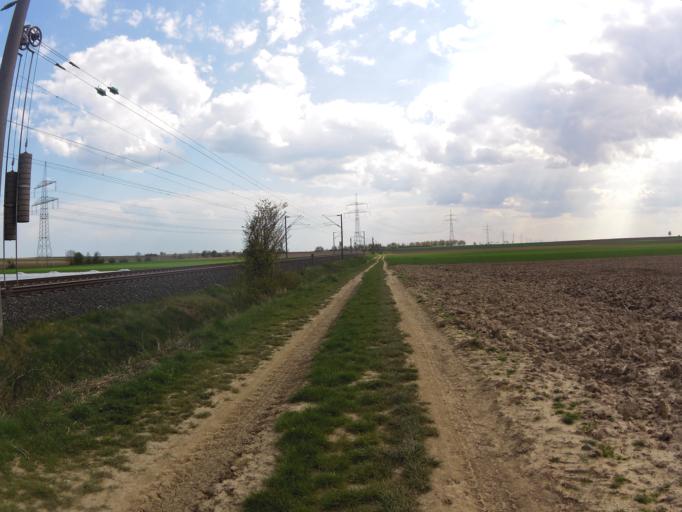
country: DE
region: Bavaria
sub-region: Regierungsbezirk Unterfranken
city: Oberpleichfeld
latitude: 49.8700
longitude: 10.0991
